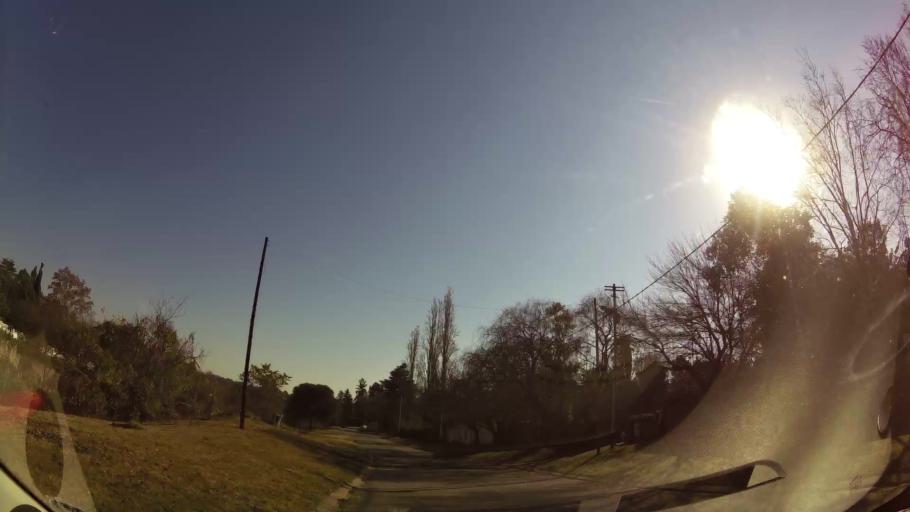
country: ZA
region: Gauteng
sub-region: City of Johannesburg Metropolitan Municipality
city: Midrand
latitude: -26.0652
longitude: 28.0507
